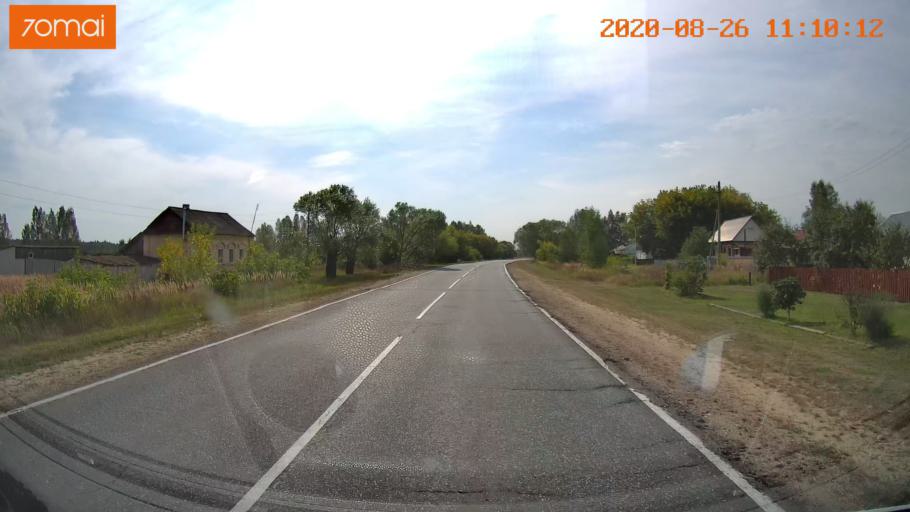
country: RU
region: Rjazan
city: Izhevskoye
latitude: 54.4808
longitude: 41.1263
